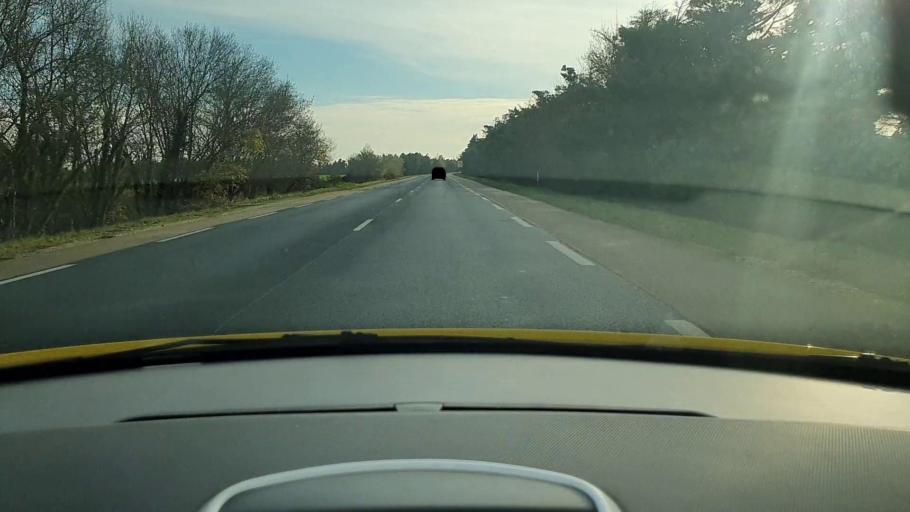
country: FR
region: Languedoc-Roussillon
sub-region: Departement du Gard
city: Fourques
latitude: 43.7044
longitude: 4.5655
